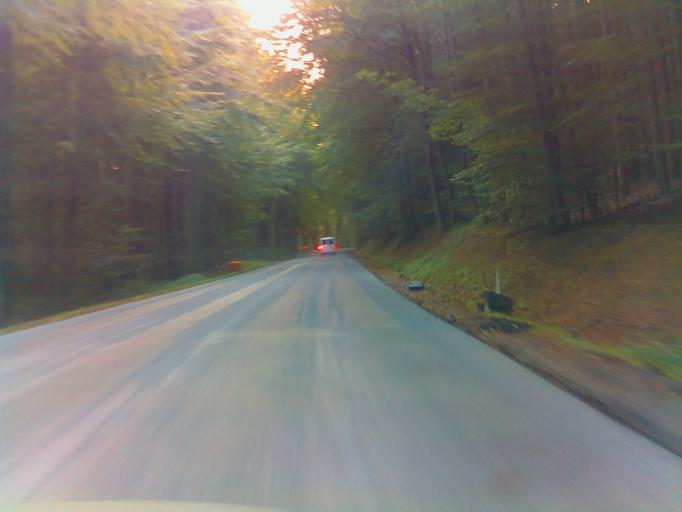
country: DE
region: Hesse
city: Michelstadt
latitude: 49.6584
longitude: 9.0335
